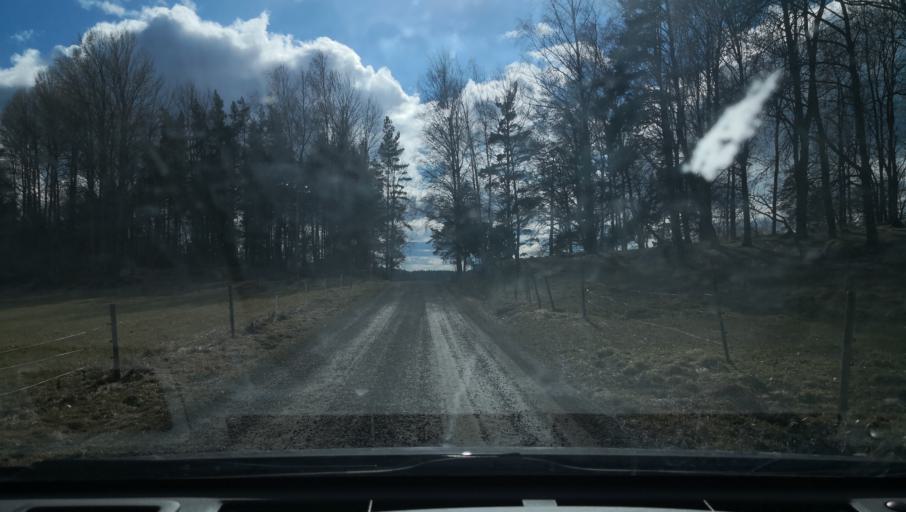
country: SE
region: OErebro
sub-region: Lindesbergs Kommun
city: Fellingsbro
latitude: 59.4151
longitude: 15.6779
